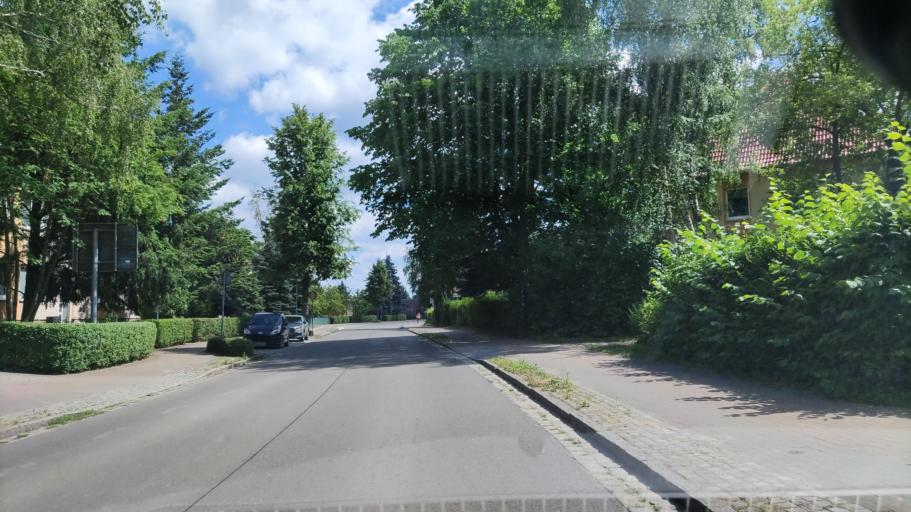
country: DE
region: Mecklenburg-Vorpommern
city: Hagenow
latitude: 53.4357
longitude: 11.1818
